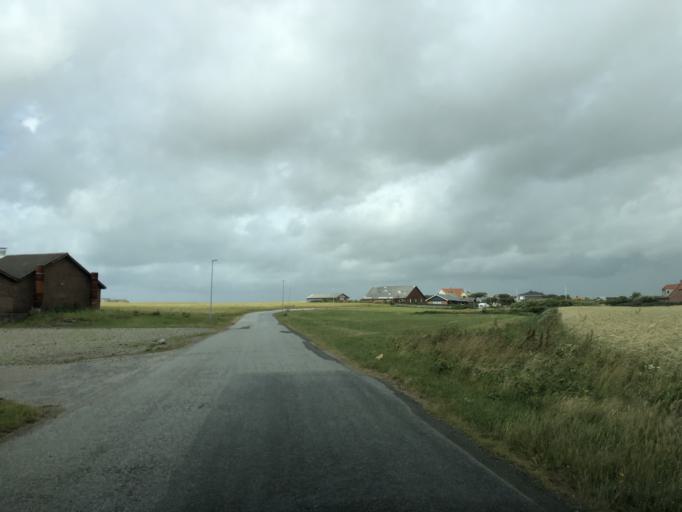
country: DK
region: Central Jutland
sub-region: Lemvig Kommune
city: Harboore
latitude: 56.4787
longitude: 8.1403
